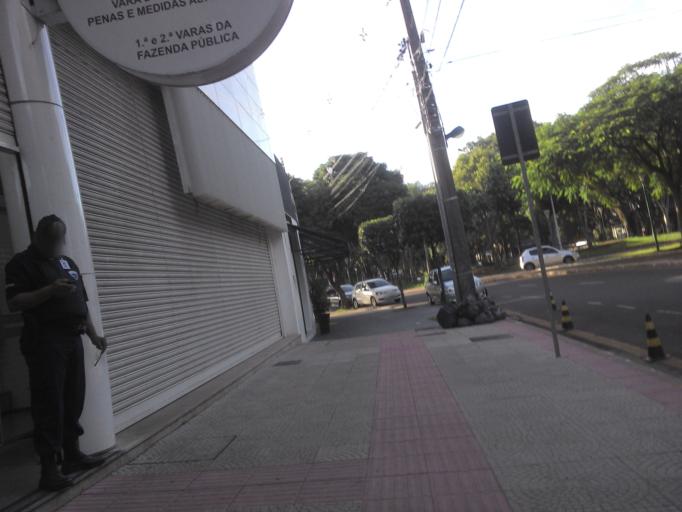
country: BR
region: Parana
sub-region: Maringa
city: Maringa
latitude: -23.4295
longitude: -51.9367
